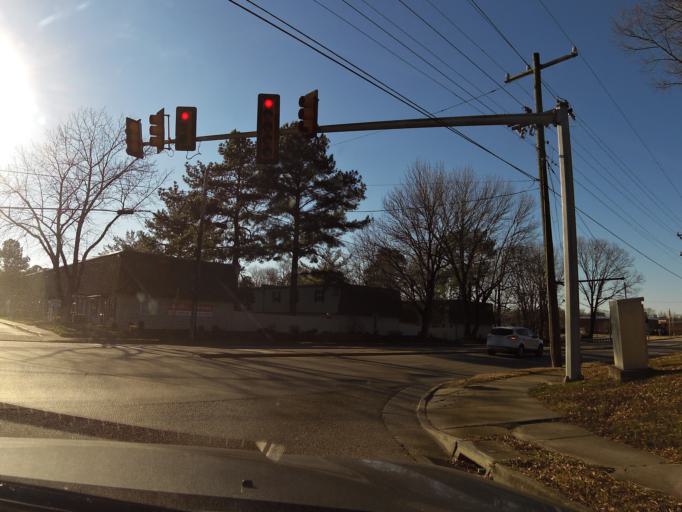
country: US
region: Virginia
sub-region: City of Hopewell
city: Hopewell
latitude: 37.2929
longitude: -77.2900
